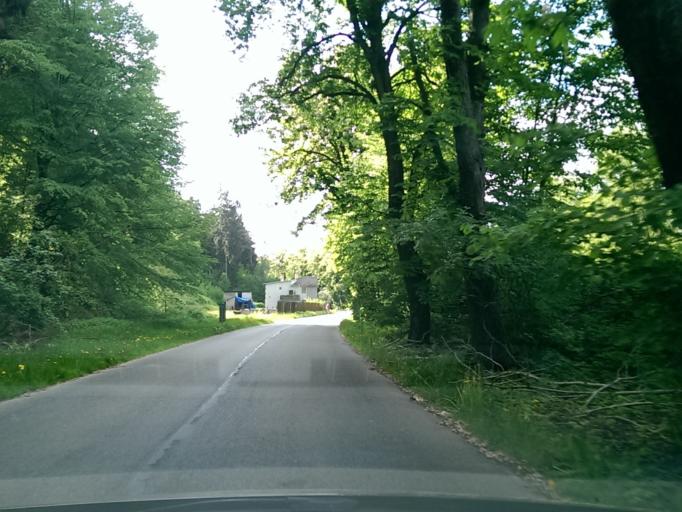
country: CZ
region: Central Bohemia
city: Bakov nad Jizerou
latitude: 50.4920
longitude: 14.9127
